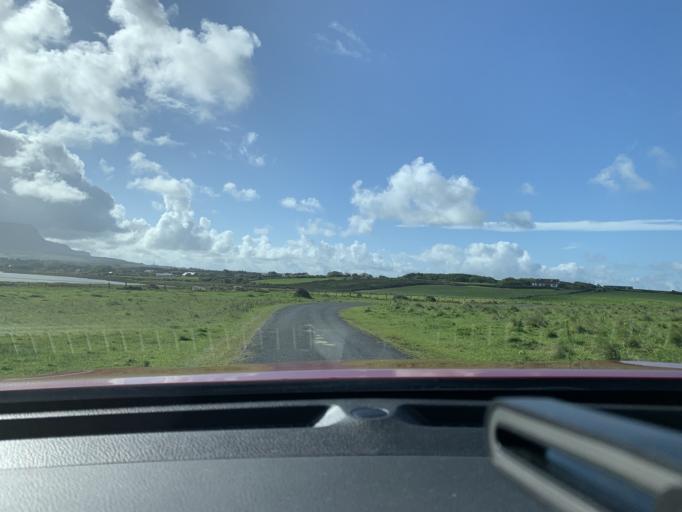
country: IE
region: Connaught
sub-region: Sligo
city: Strandhill
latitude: 54.4004
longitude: -8.5640
